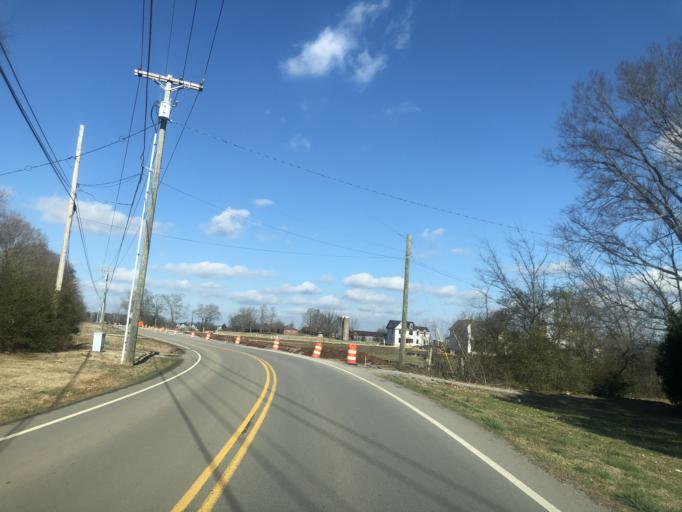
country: US
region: Tennessee
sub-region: Rutherford County
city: Smyrna
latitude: 35.8786
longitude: -86.4967
